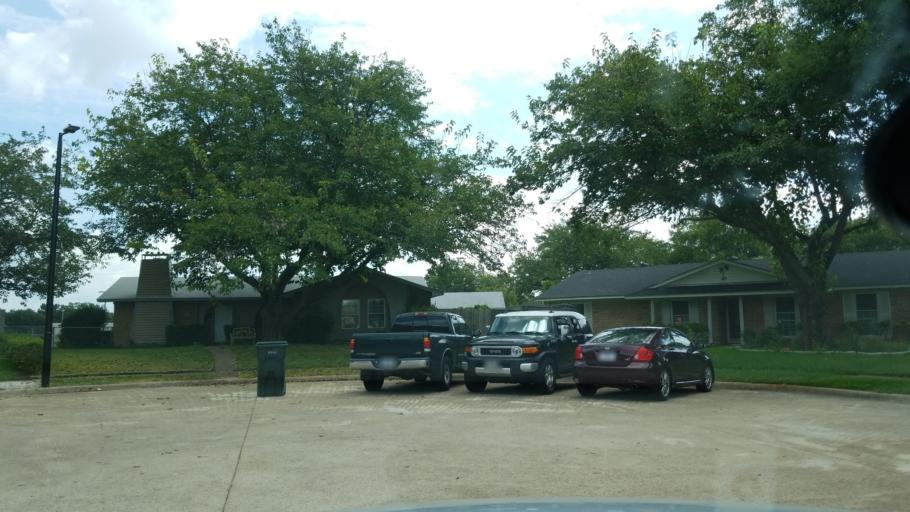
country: US
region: Texas
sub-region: Dallas County
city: Garland
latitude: 32.9287
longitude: -96.6515
